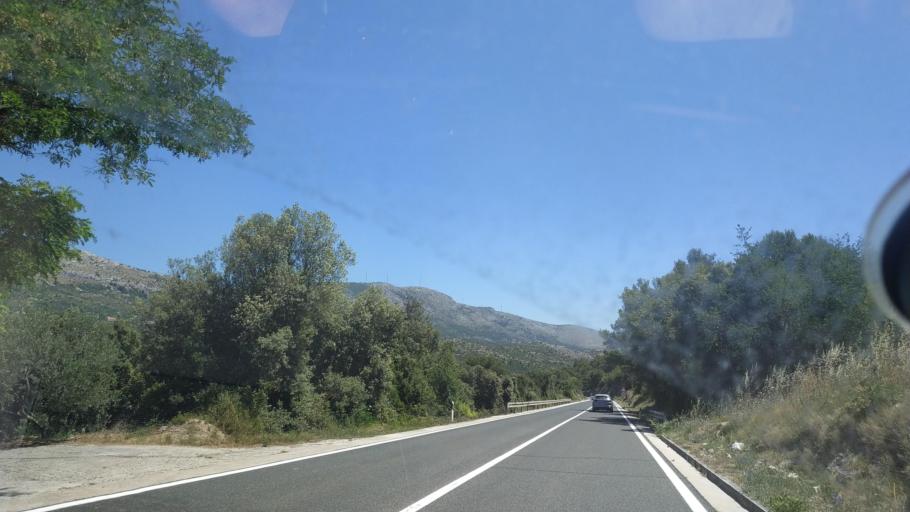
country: HR
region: Sibensko-Kniniska
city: Primosten
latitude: 43.6303
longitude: 15.9692
